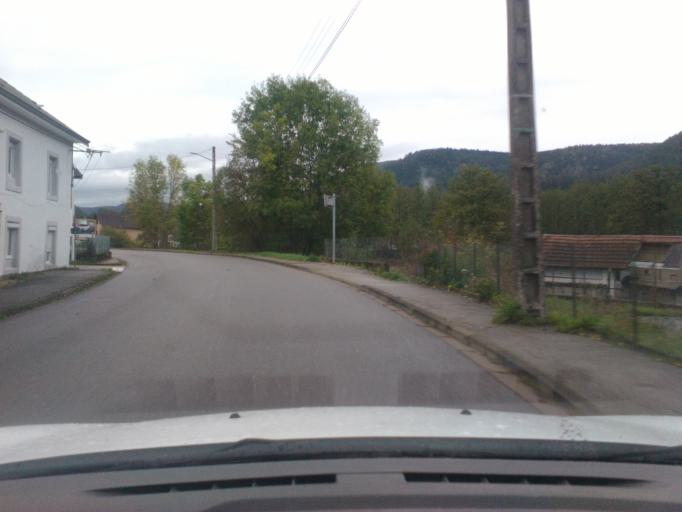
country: FR
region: Lorraine
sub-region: Departement des Vosges
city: Saint-Die-des-Vosges
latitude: 48.2891
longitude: 6.9223
